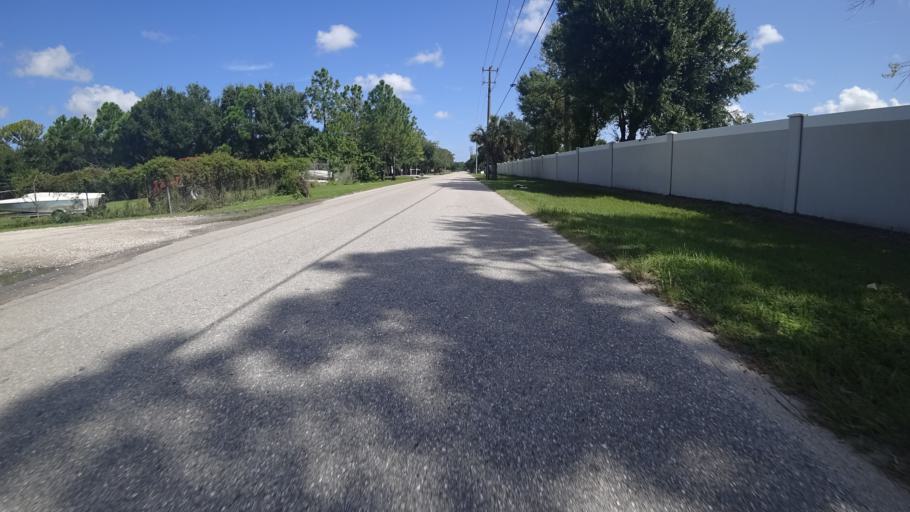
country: US
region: Florida
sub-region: Manatee County
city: Whitfield
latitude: 27.4334
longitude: -82.5383
